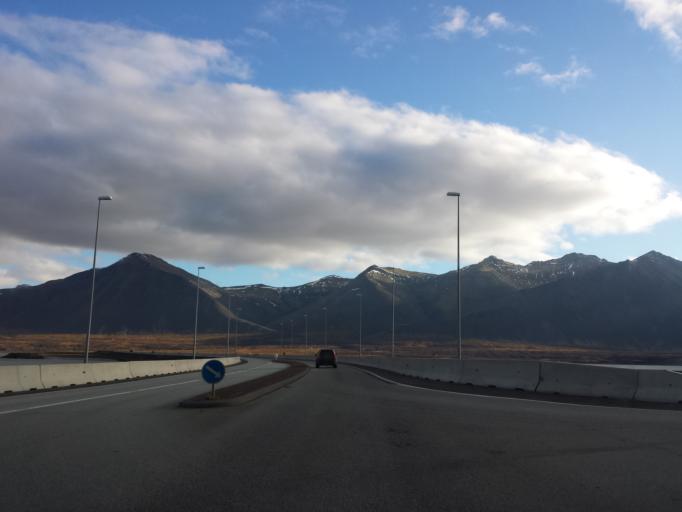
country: IS
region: West
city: Borgarnes
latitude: 64.5401
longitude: -21.9071
